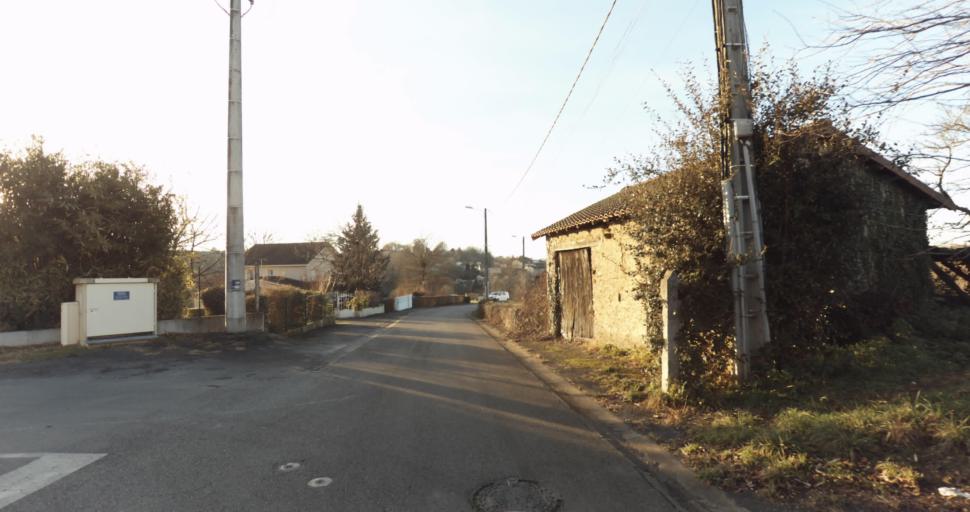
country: FR
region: Limousin
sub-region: Departement de la Haute-Vienne
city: Aixe-sur-Vienne
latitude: 45.7937
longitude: 1.1422
